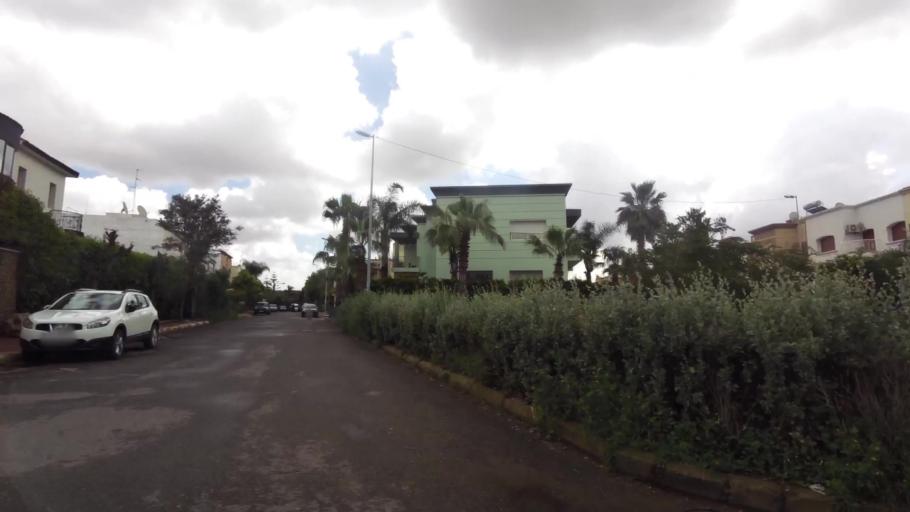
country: MA
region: Grand Casablanca
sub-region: Nouaceur
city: Bouskoura
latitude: 33.5163
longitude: -7.6435
